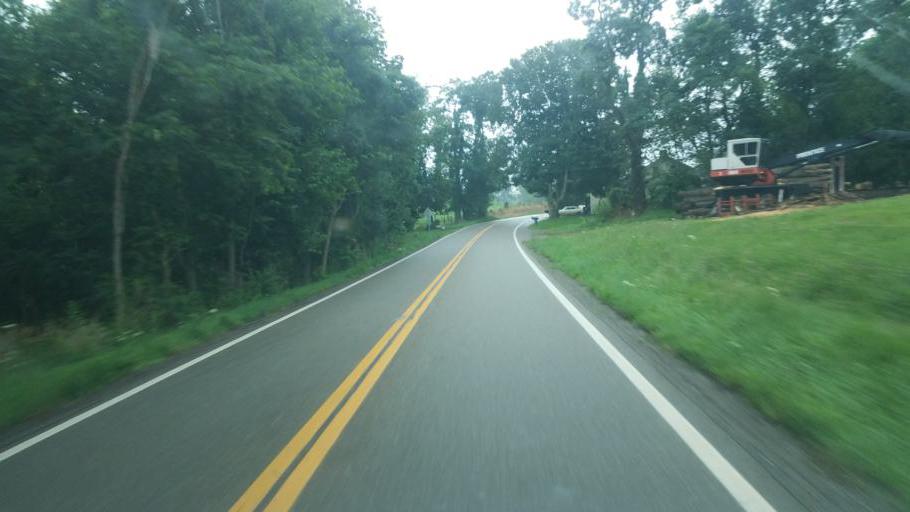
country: US
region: Ohio
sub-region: Tuscarawas County
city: Rockford
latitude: 40.4498
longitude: -81.1676
